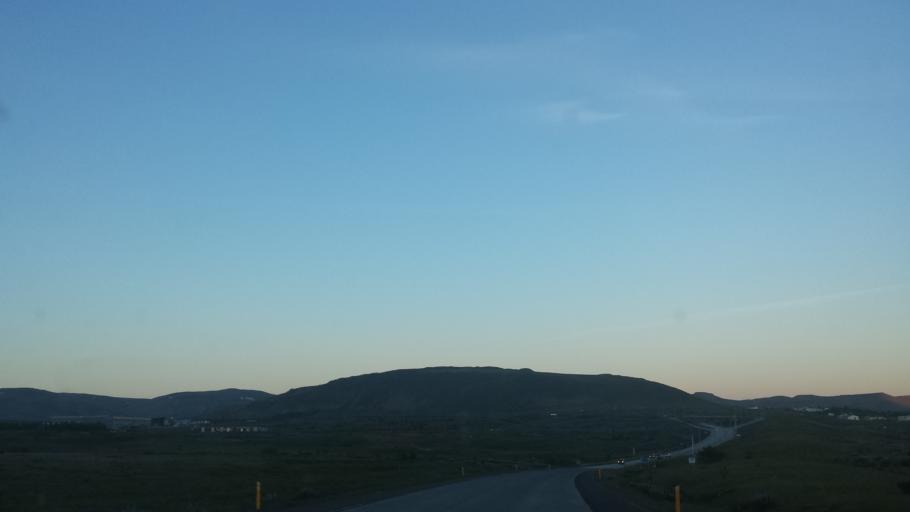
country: IS
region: Capital Region
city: Mosfellsbaer
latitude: 64.1909
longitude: -21.6895
